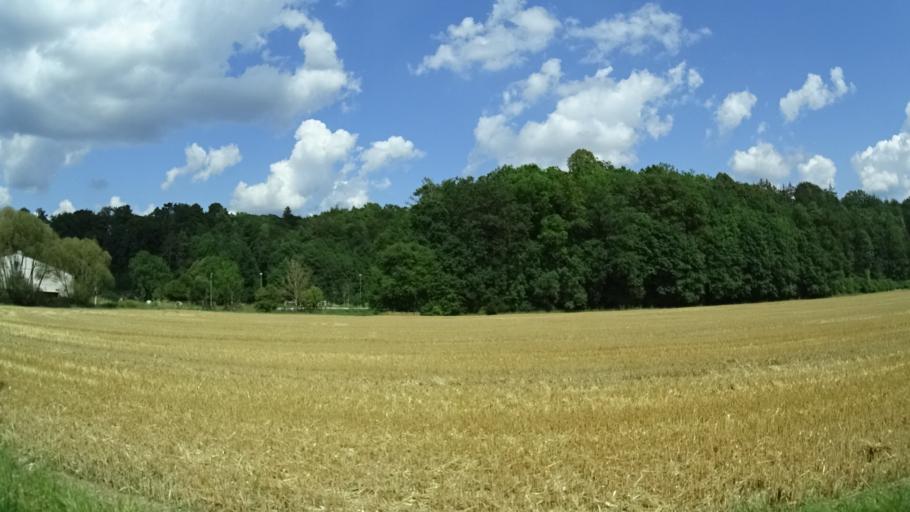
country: DE
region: Thuringia
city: Veilsdorf
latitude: 50.4046
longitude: 10.8134
